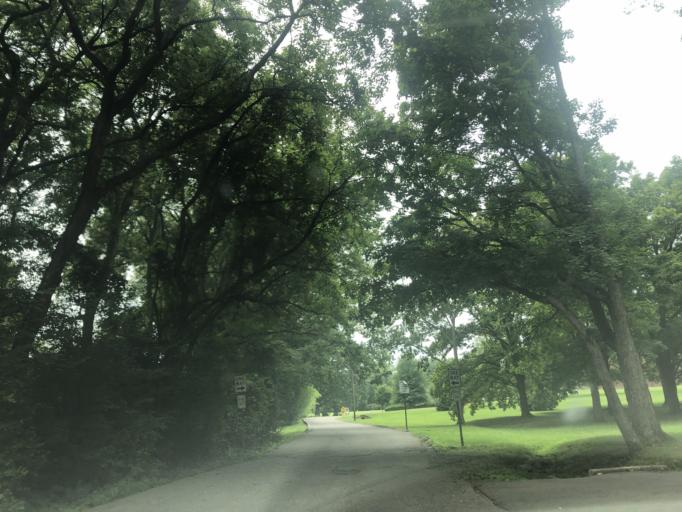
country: US
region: Tennessee
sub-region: Davidson County
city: Oak Hill
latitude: 36.0966
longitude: -86.7835
